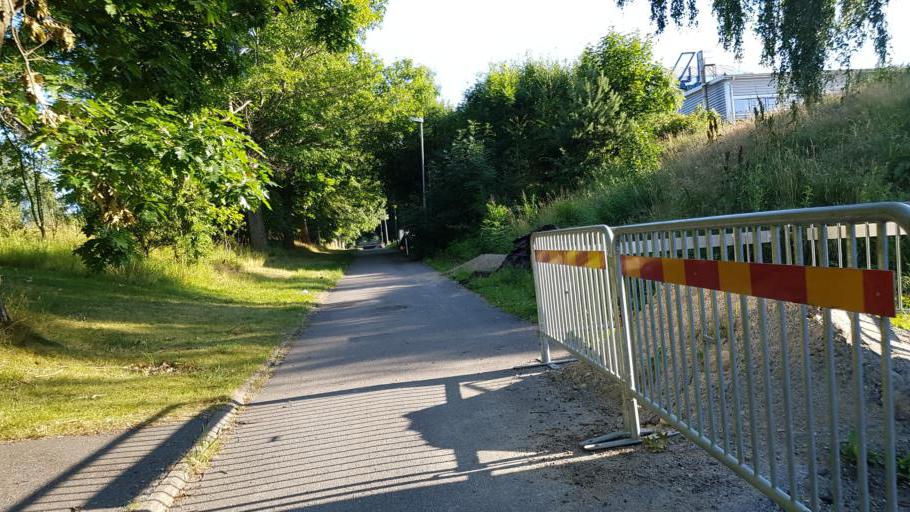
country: SE
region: Vaestra Goetaland
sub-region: Harryda Kommun
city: Molnlycke
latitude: 57.6701
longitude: 12.0983
